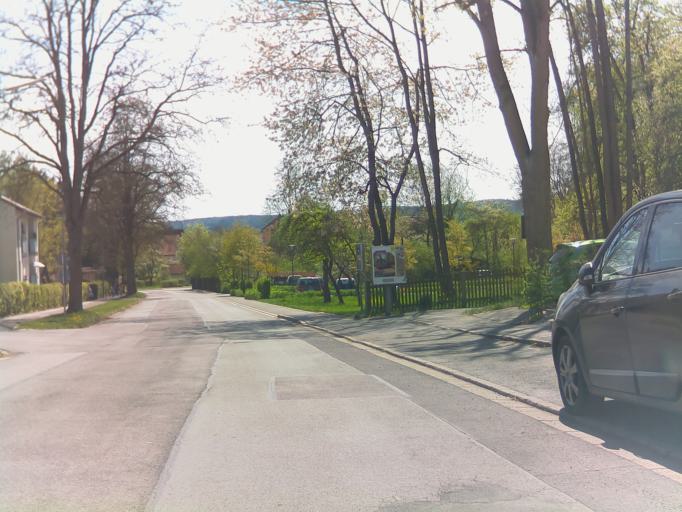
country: DE
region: Thuringia
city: Veilsdorf
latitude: 50.3440
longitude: 10.7770
